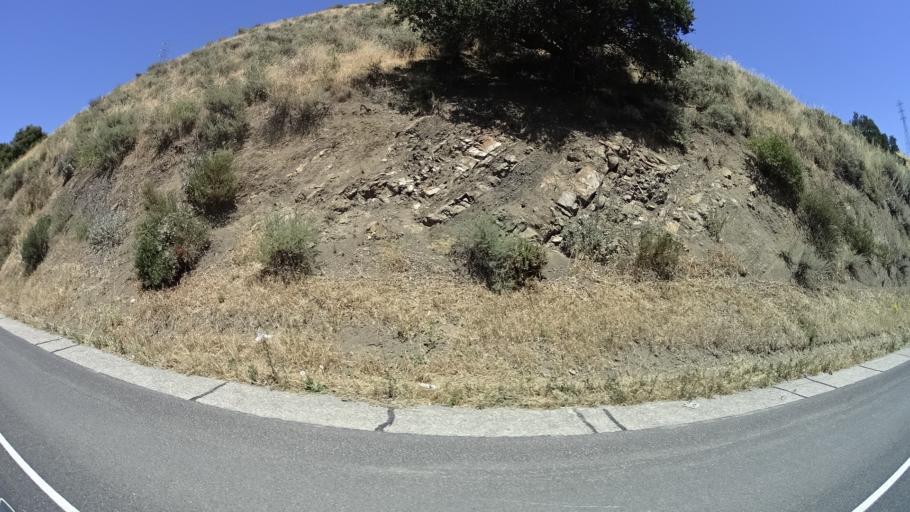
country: US
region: California
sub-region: San Luis Obispo County
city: San Luis Obispo
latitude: 35.3207
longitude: -120.6212
